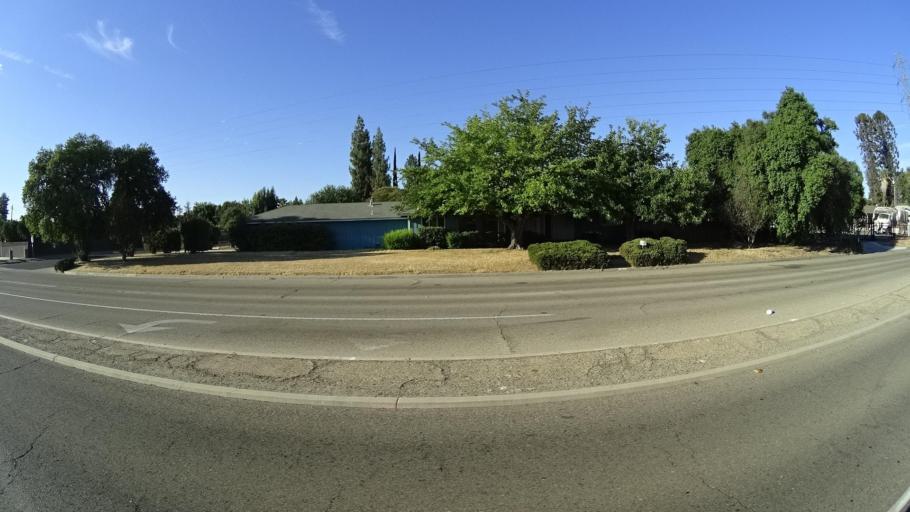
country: US
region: California
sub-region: Fresno County
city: Sunnyside
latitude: 36.7506
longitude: -119.7049
